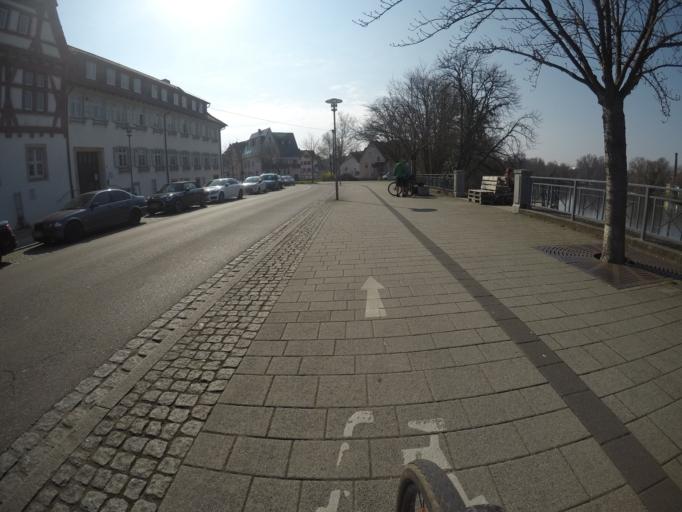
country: DE
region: Baden-Wuerttemberg
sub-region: Regierungsbezirk Stuttgart
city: Nurtingen
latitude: 48.6271
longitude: 9.3340
